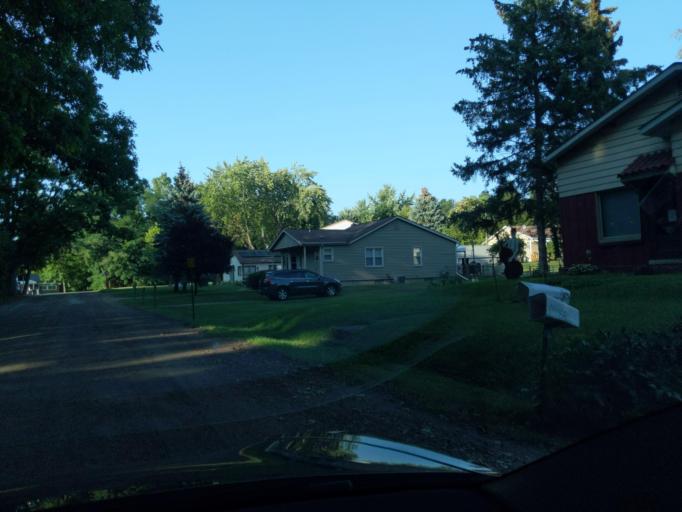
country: US
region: Michigan
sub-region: Livingston County
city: Whitmore Lake
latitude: 42.4421
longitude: -83.7503
